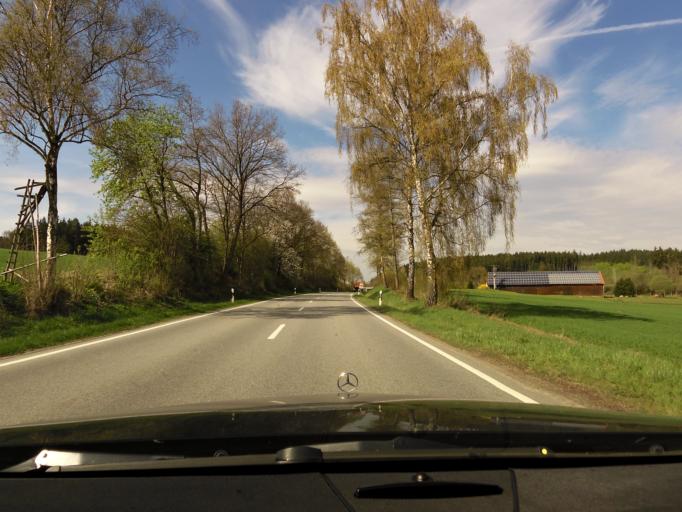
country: DE
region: Bavaria
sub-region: Upper Palatinate
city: Schierling
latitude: 48.7941
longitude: 12.1720
